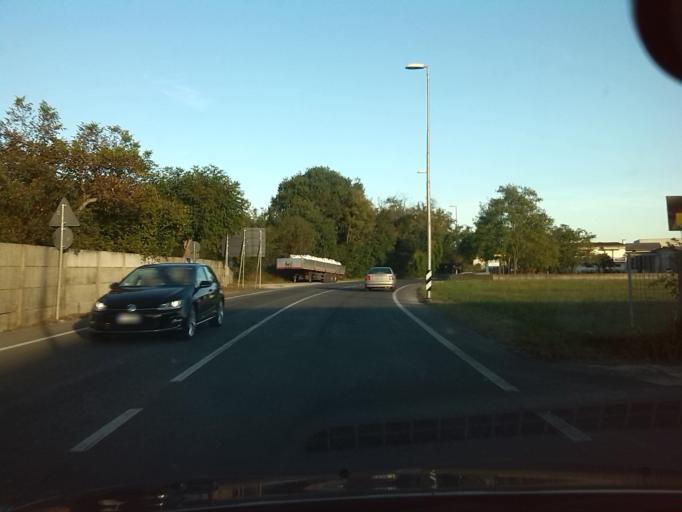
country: IT
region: Friuli Venezia Giulia
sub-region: Provincia di Udine
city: Basaldella
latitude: 46.0257
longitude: 13.2170
